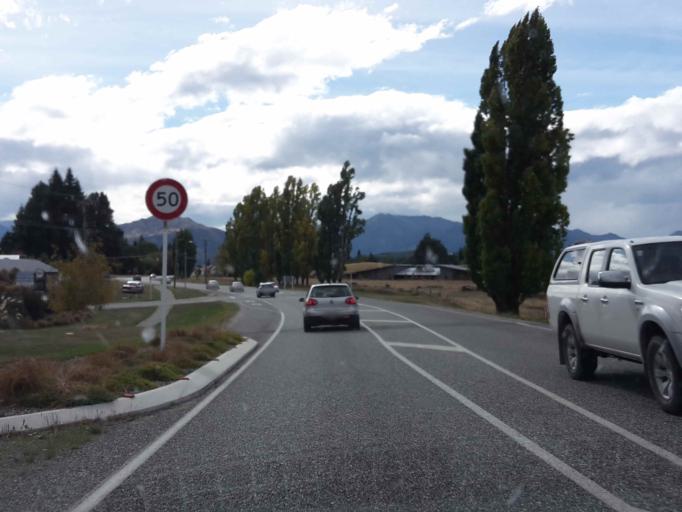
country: NZ
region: Otago
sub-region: Queenstown-Lakes District
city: Wanaka
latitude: -44.7124
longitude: 169.1370
